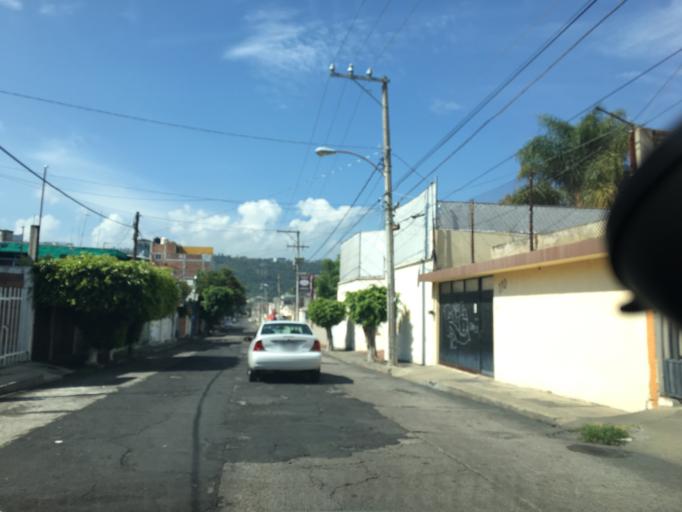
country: MX
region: Michoacan
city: Morelia
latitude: 19.6937
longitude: -101.1696
